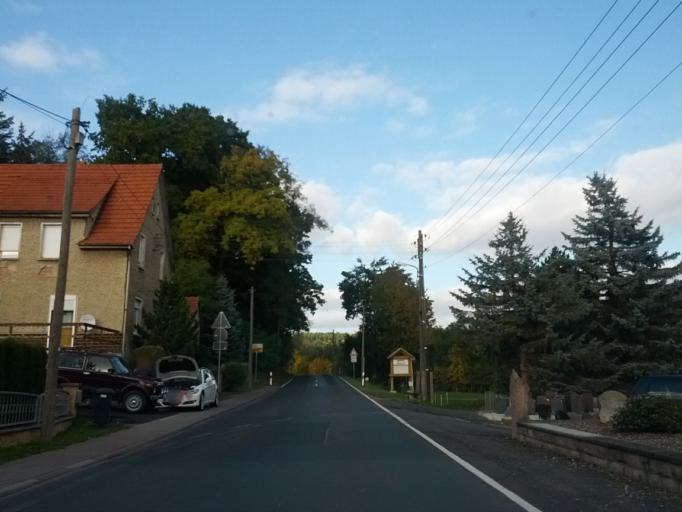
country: DE
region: Thuringia
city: Marksuhl
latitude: 50.9319
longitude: 10.1540
